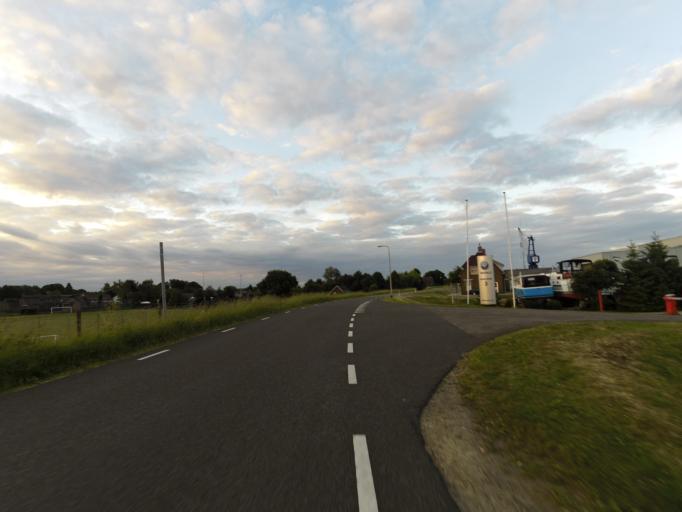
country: NL
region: Gelderland
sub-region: Gemeente Duiven
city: Duiven
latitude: 51.8780
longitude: 5.9909
